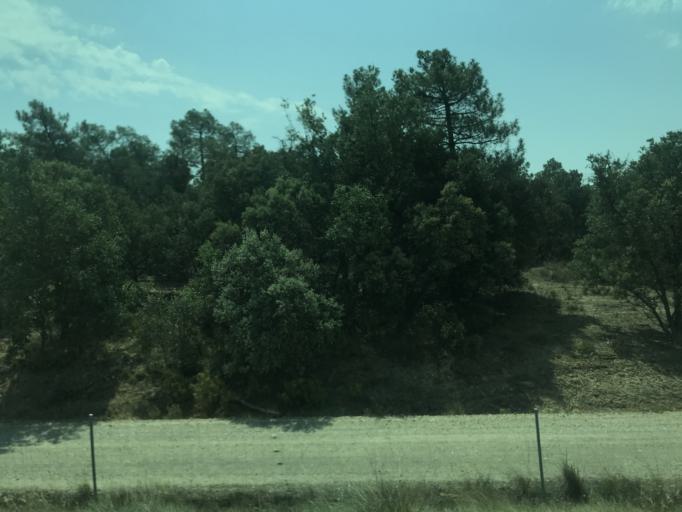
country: ES
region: Castille and Leon
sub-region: Provincia de Burgos
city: Aranda de Duero
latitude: 41.7061
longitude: -3.6978
